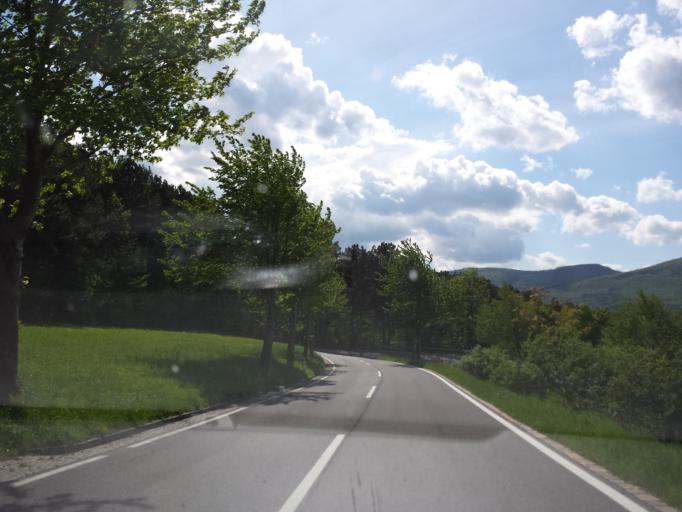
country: AT
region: Lower Austria
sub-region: Politischer Bezirk Baden
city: Hernstein
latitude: 47.8901
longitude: 16.1096
